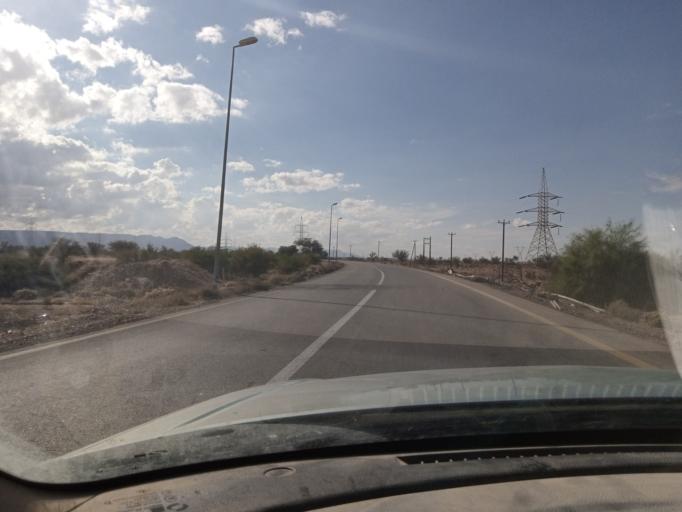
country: LY
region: Sha`biyat al Jabal al Gharbi
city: Yafran
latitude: 32.1197
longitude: 12.4028
